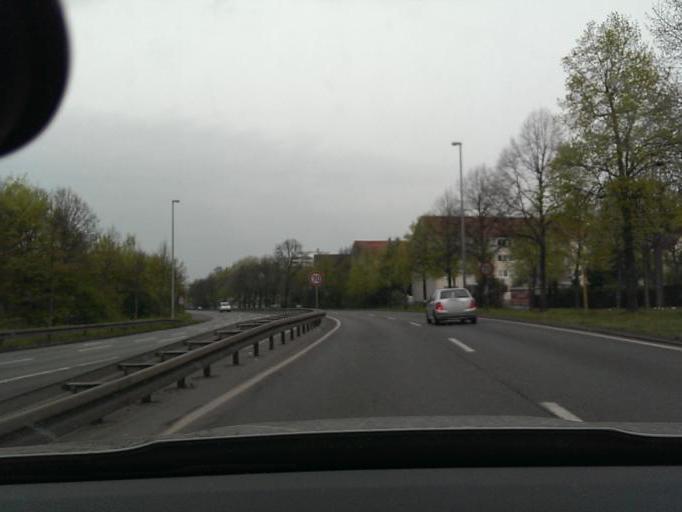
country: DE
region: Lower Saxony
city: Auf der Horst
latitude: 52.4079
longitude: 9.6546
